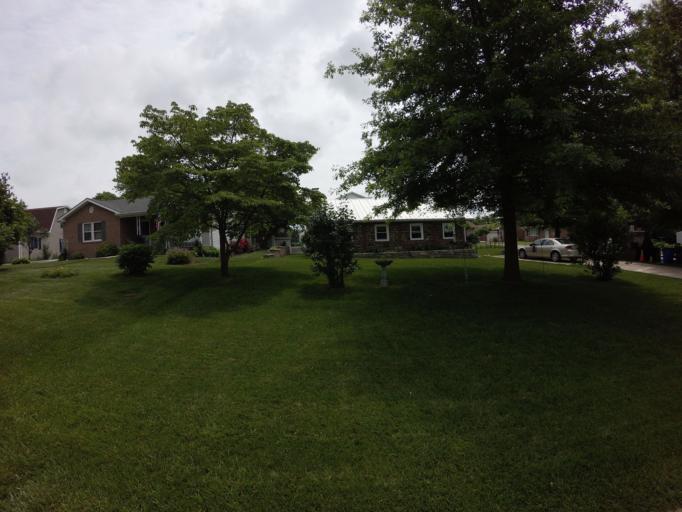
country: US
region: Maryland
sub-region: Frederick County
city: Brunswick
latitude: 39.3188
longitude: -77.6209
